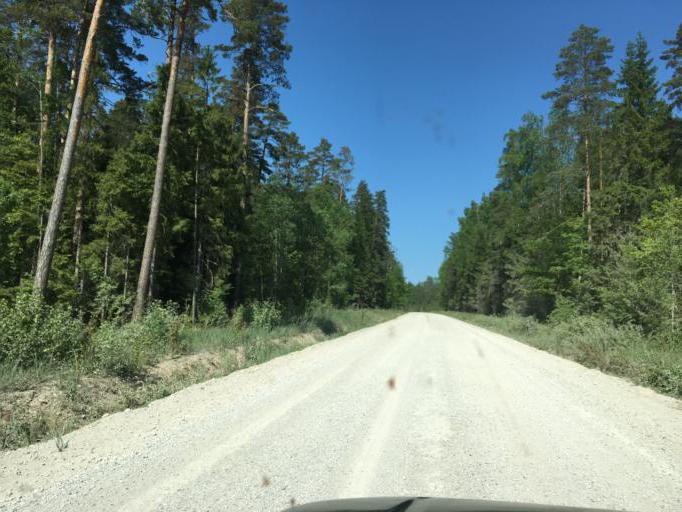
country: LV
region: Dundaga
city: Dundaga
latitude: 57.4352
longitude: 22.3143
